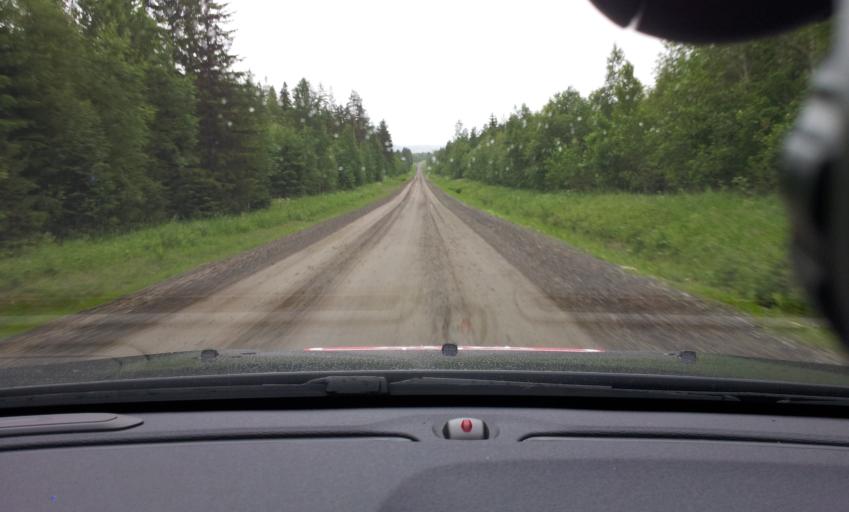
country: SE
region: Jaemtland
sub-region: Ragunda Kommun
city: Hammarstrand
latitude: 63.1371
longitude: 16.3155
